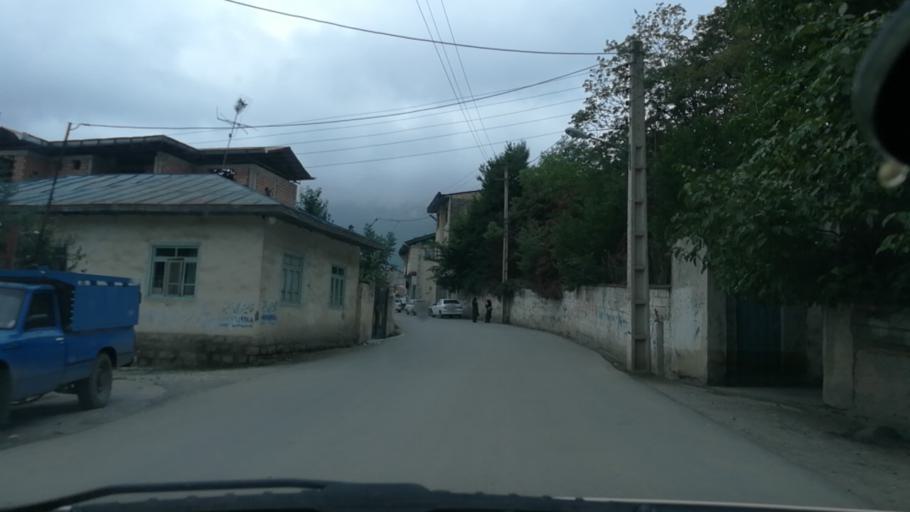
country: IR
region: Mazandaran
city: `Abbasabad
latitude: 36.5035
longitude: 51.1518
